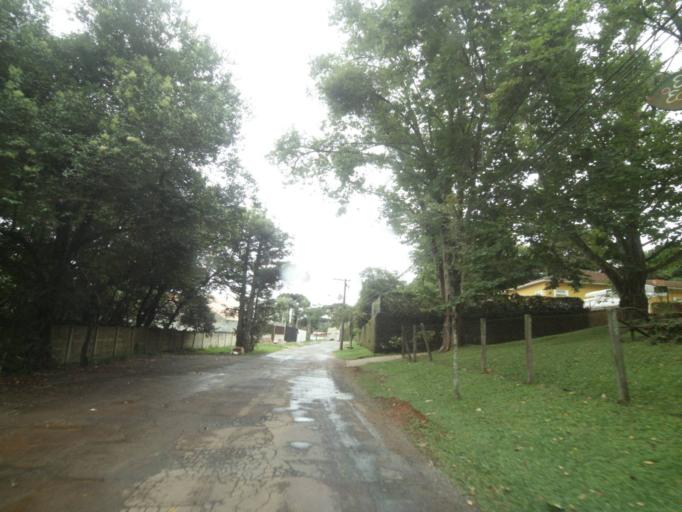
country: BR
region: Parana
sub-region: Curitiba
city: Curitiba
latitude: -25.4506
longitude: -49.3245
